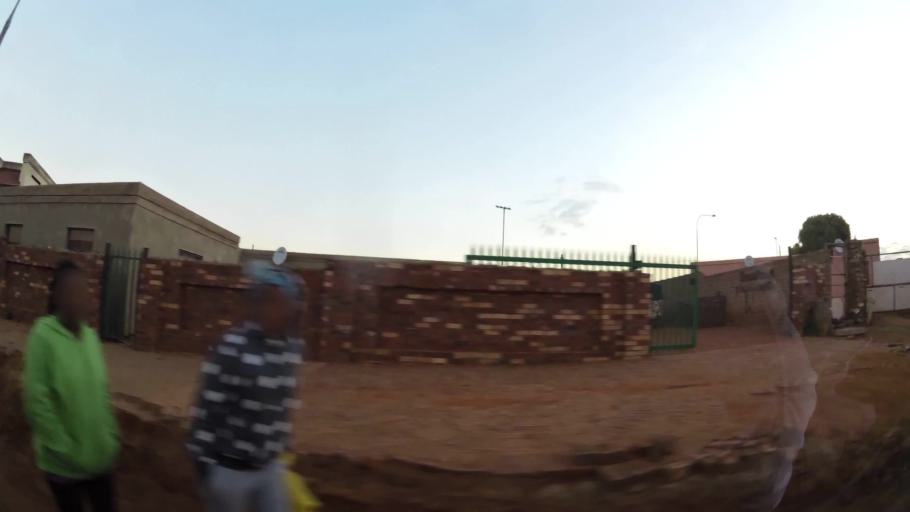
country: ZA
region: Gauteng
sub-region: West Rand District Municipality
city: Randfontein
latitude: -26.2112
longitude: 27.7079
